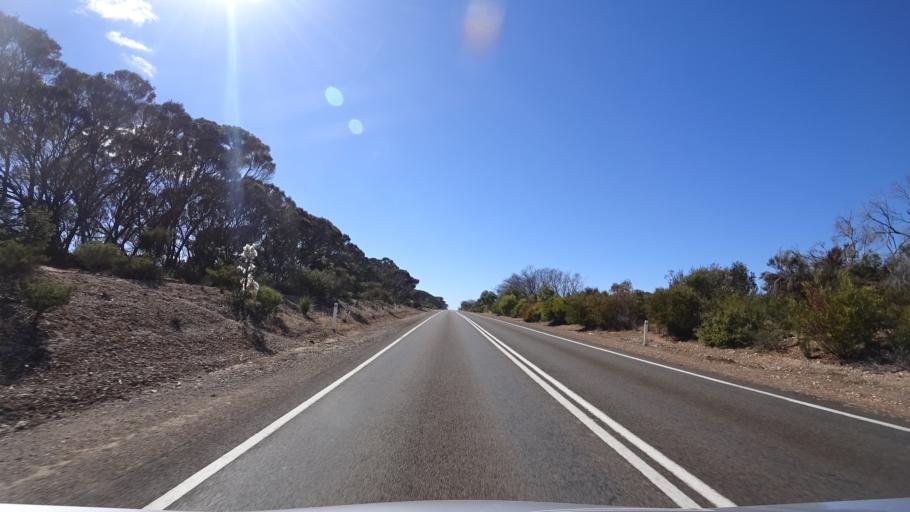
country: AU
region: South Australia
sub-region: Kangaroo Island
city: Kingscote
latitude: -35.7627
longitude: 137.6120
